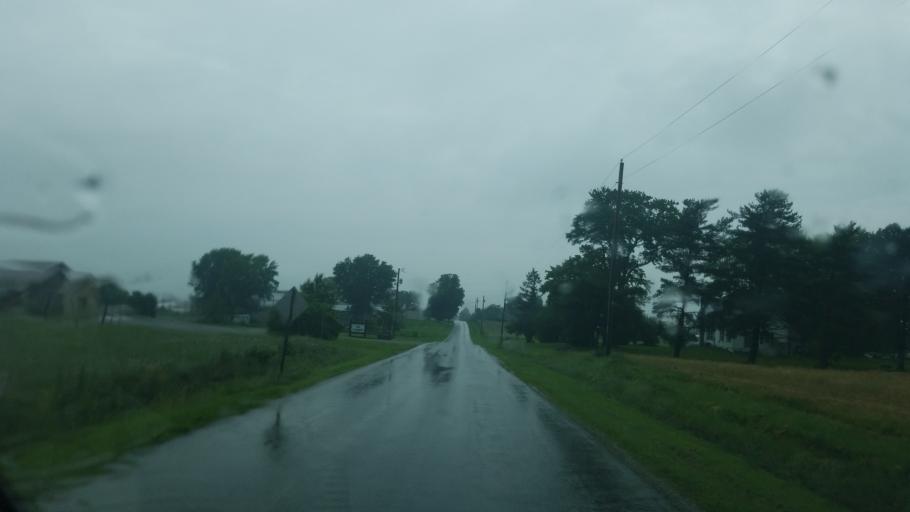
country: US
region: Ohio
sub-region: Huron County
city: Greenwich
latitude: 41.0546
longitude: -82.5853
